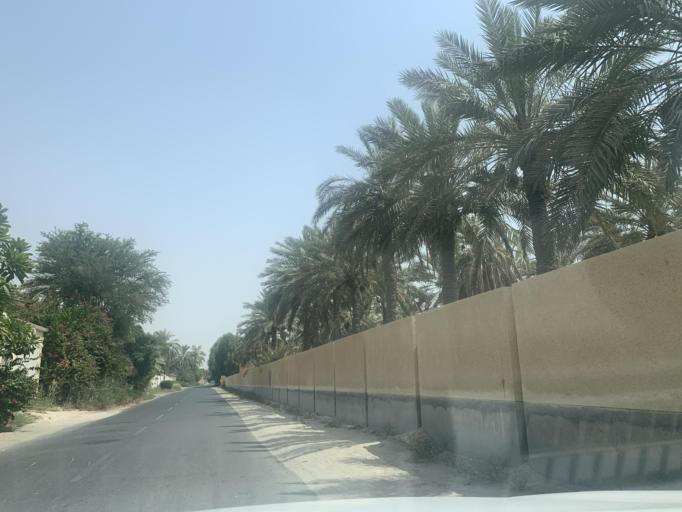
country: BH
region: Manama
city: Jidd Hafs
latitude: 26.2273
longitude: 50.4660
